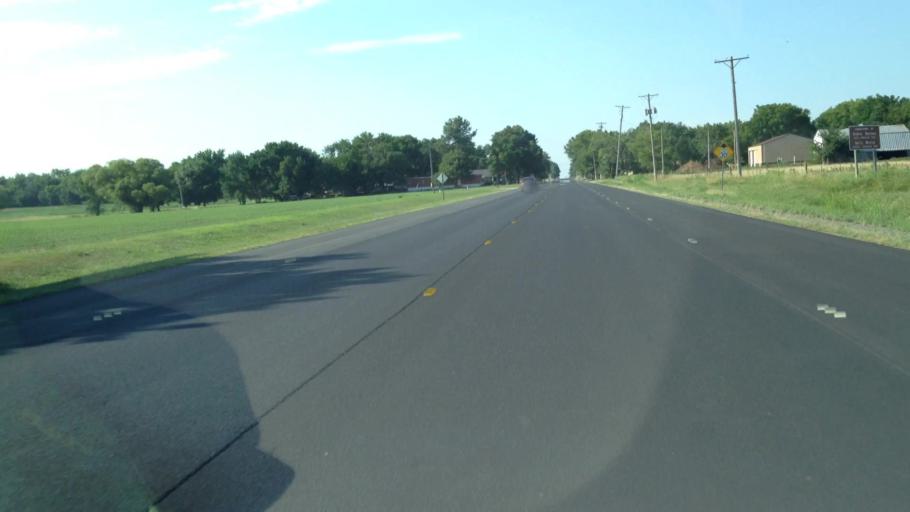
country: US
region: Kansas
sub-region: Allen County
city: Iola
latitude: 37.9082
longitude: -95.1702
